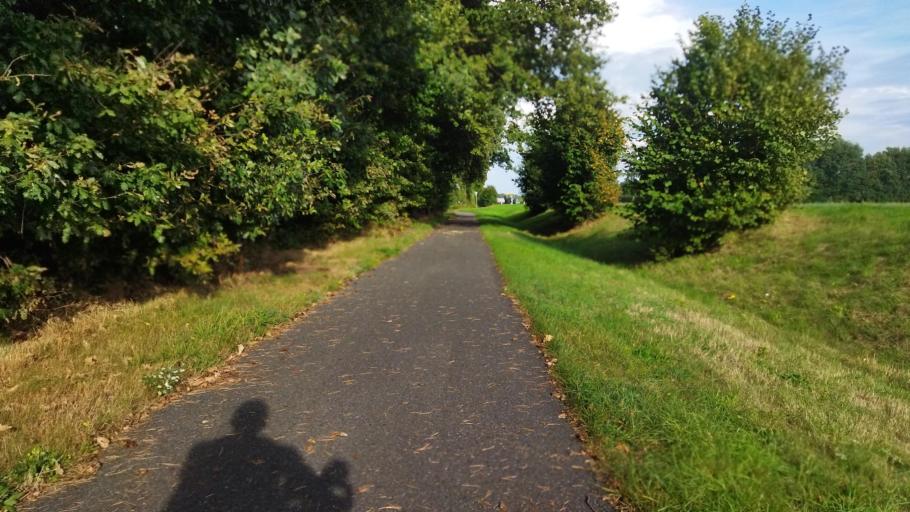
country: DE
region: North Rhine-Westphalia
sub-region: Regierungsbezirk Munster
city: Ostbevern
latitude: 52.0516
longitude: 7.9028
